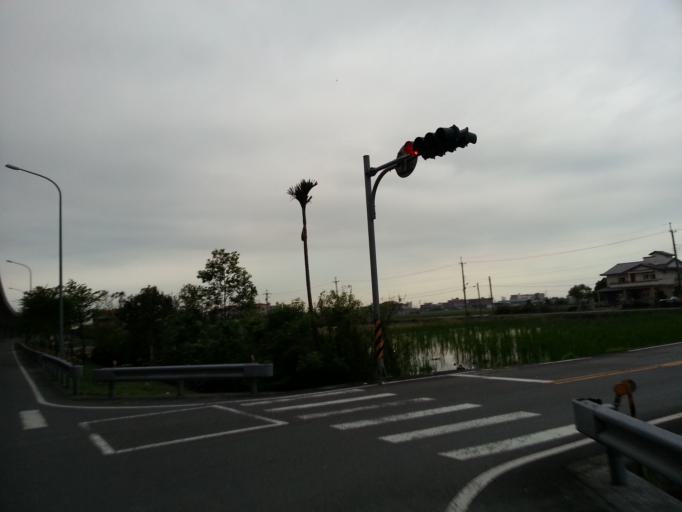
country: TW
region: Taiwan
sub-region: Yilan
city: Yilan
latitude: 24.6371
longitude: 121.8058
